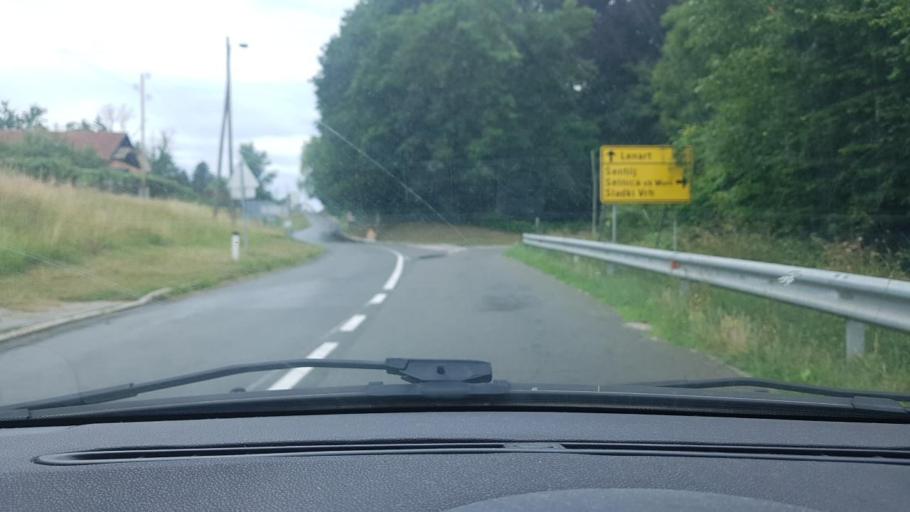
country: AT
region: Styria
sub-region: Politischer Bezirk Suedoststeiermark
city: Mureck
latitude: 46.6977
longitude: 15.7868
